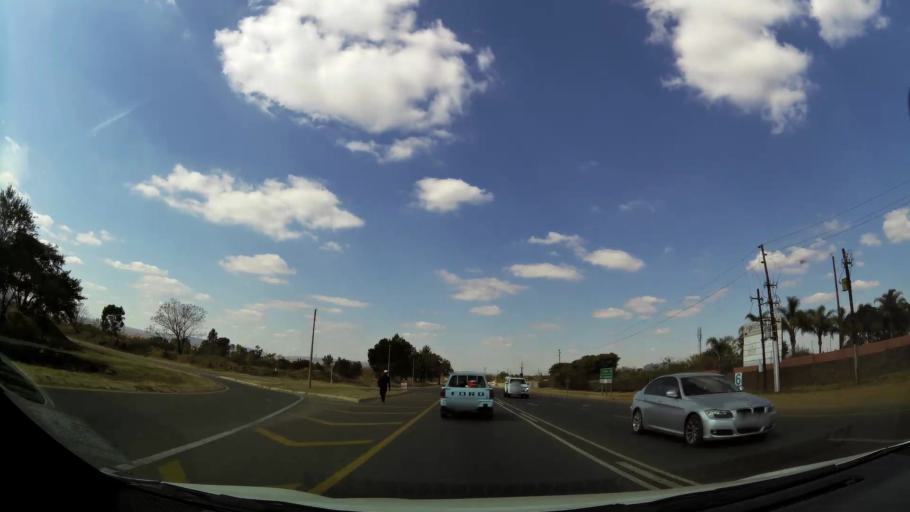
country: ZA
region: Gauteng
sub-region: City of Tshwane Metropolitan Municipality
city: Pretoria
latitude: -25.7397
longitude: 28.3353
